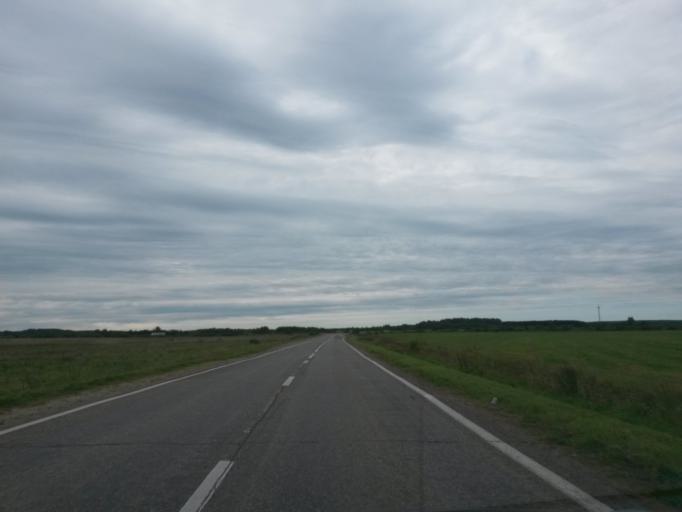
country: RU
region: Jaroslavl
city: Gavrilov-Yam
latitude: 57.3127
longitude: 39.8830
